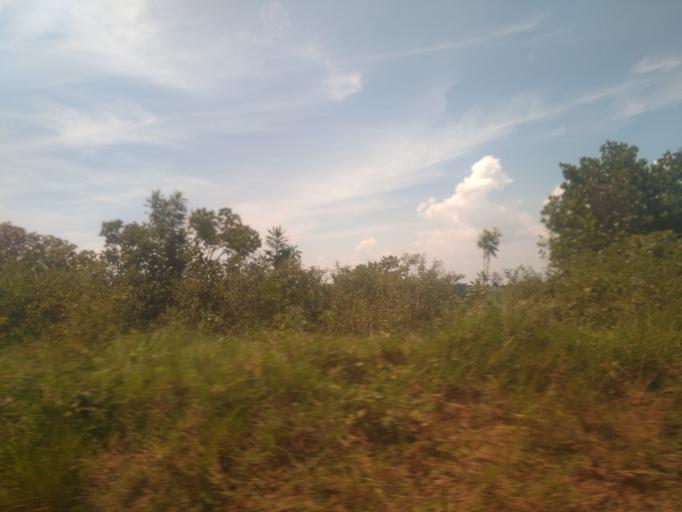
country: UG
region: Central Region
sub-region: Wakiso District
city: Entebbe
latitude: 0.0388
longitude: 32.4370
